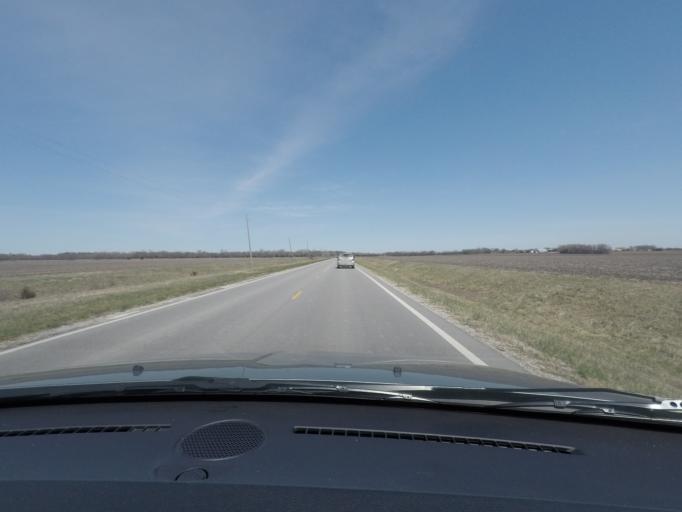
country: US
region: Kansas
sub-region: Lyon County
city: Emporia
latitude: 38.4422
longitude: -96.1706
